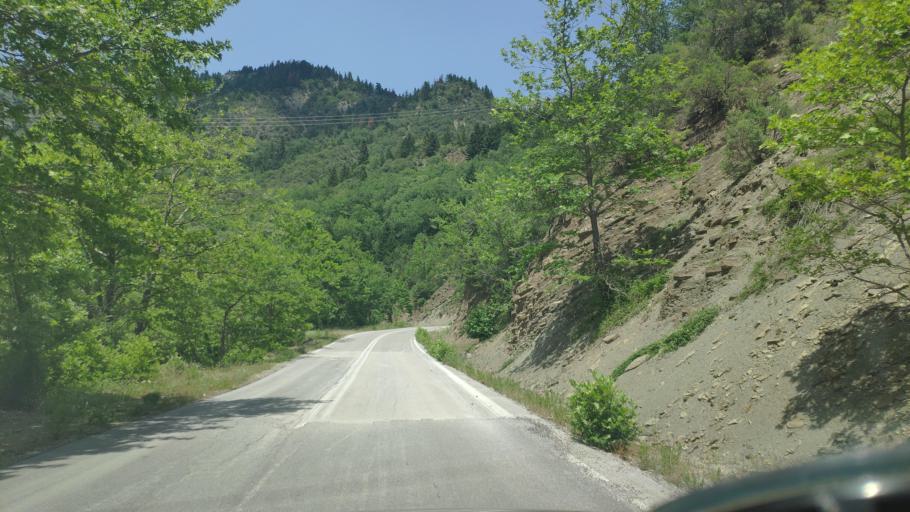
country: GR
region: Thessaly
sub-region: Nomos Kardhitsas
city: Anthiro
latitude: 39.2693
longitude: 21.3534
